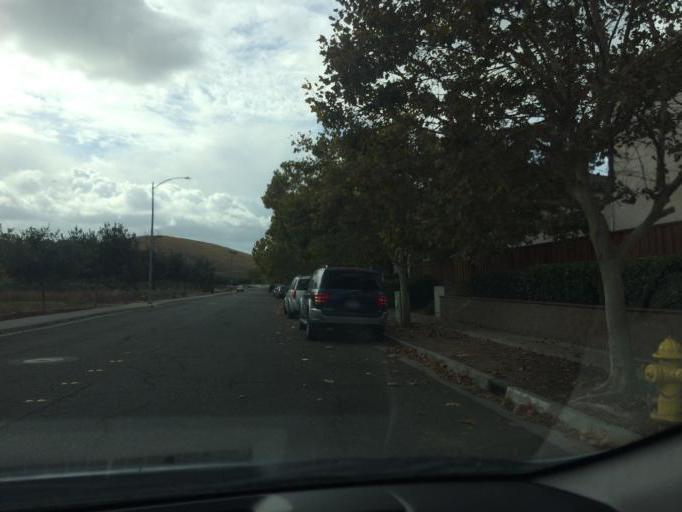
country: US
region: California
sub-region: Santa Clara County
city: Seven Trees
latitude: 37.2985
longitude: -121.8012
